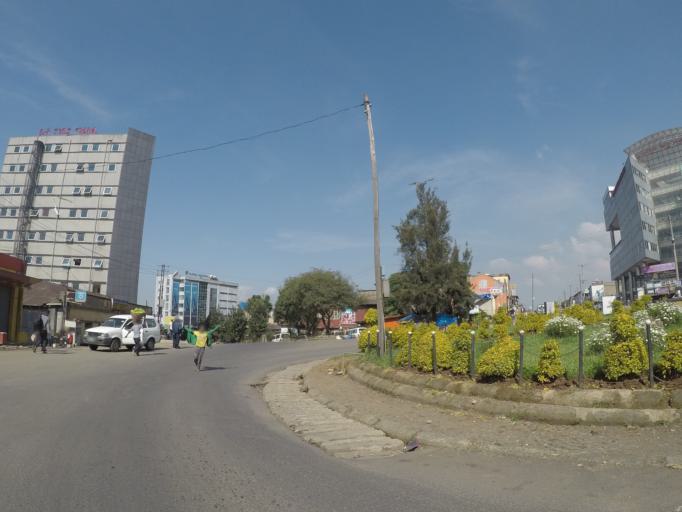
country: ET
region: Adis Abeba
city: Addis Ababa
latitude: 9.0321
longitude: 38.7474
